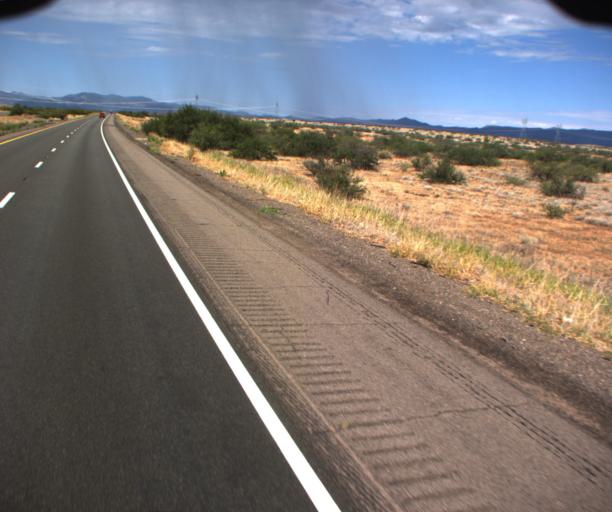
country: US
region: Arizona
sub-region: Yavapai County
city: Cordes Lakes
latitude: 34.3859
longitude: -112.0900
